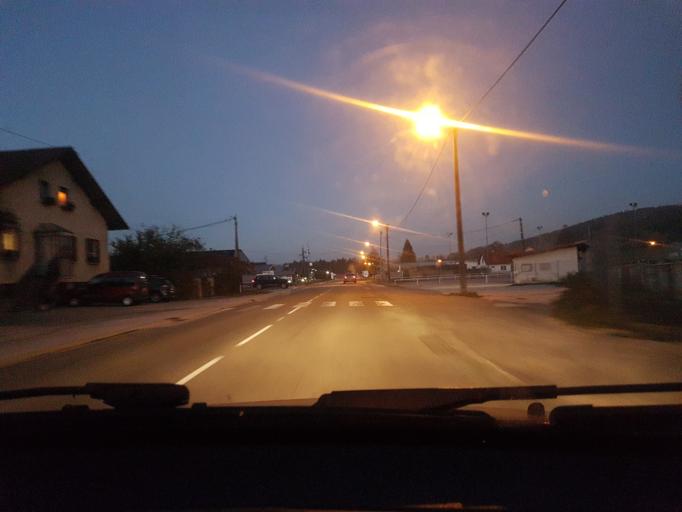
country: FR
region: Franche-Comte
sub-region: Departement du Doubs
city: Les Fins
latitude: 47.0843
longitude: 6.6371
